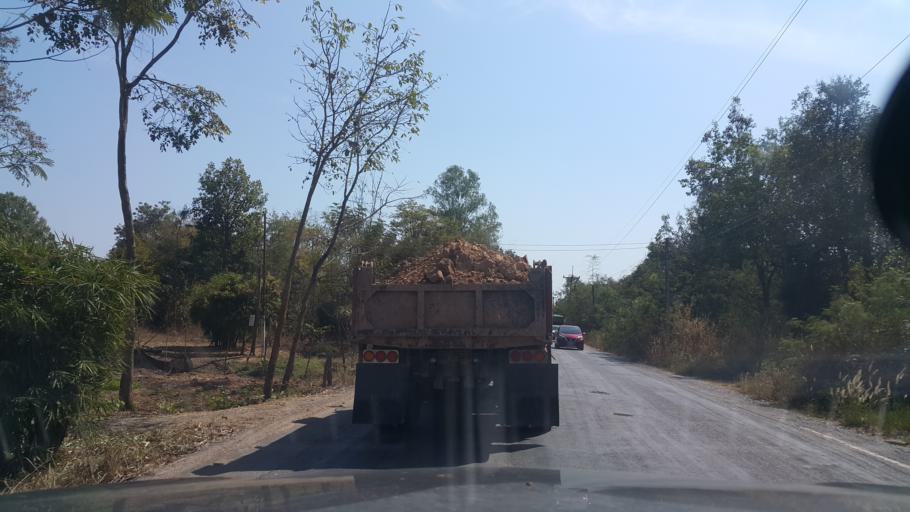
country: TH
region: Changwat Udon Thani
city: Udon Thani
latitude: 17.5134
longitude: 102.7581
